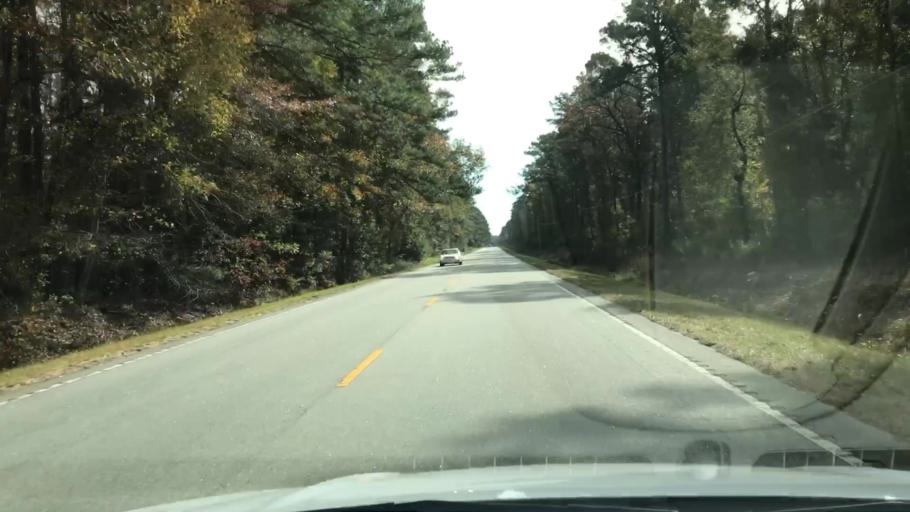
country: US
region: South Carolina
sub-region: Colleton County
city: Walterboro
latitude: 32.7917
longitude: -80.4825
